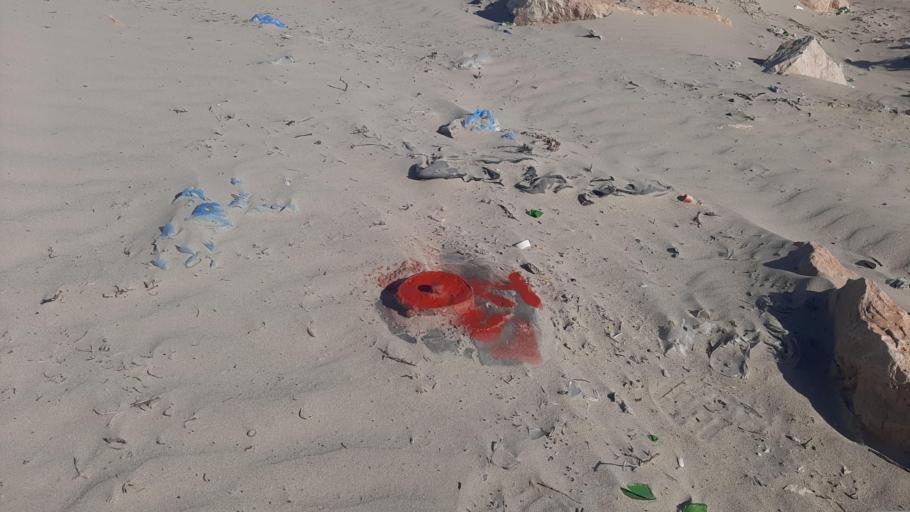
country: TN
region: Qabis
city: Gabes
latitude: 33.8841
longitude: 10.1209
